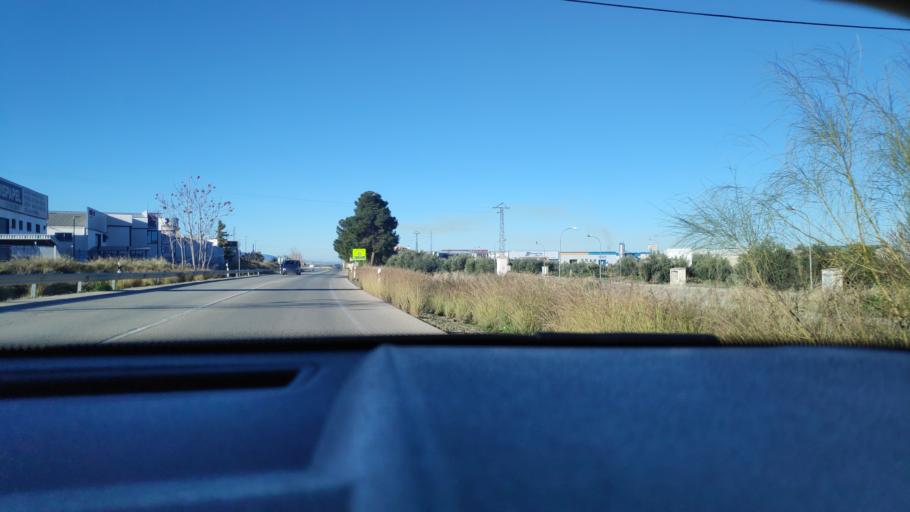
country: ES
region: Andalusia
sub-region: Provincia de Jaen
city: Mancha Real
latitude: 37.8066
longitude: -3.6150
